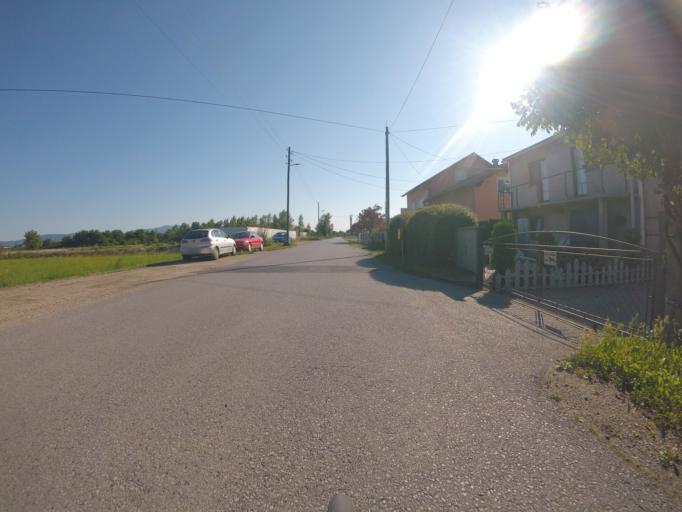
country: HR
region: Grad Zagreb
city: Lucko
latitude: 45.7535
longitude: 15.8760
